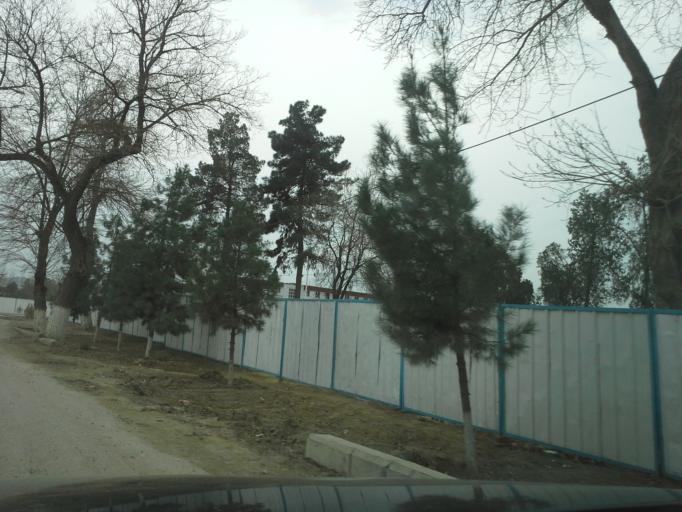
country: TM
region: Ahal
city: Ashgabat
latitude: 37.9590
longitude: 58.3426
